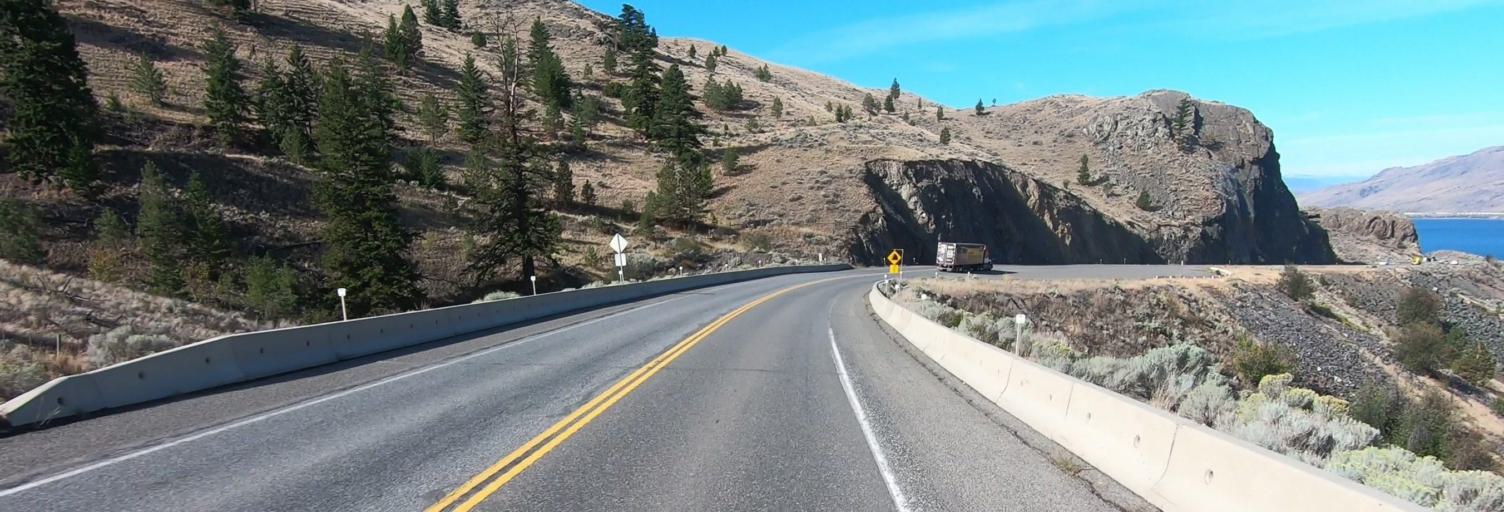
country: CA
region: British Columbia
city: Logan Lake
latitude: 50.7656
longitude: -120.7661
